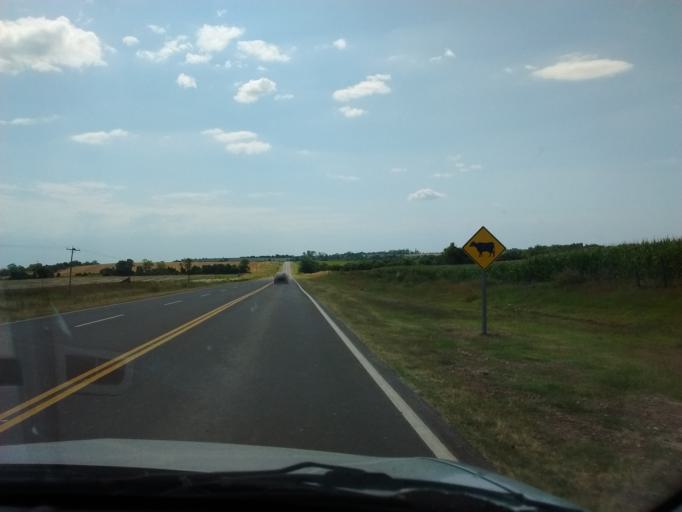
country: AR
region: Entre Rios
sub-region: Departamento de Victoria
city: Victoria
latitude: -32.6476
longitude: -60.0927
